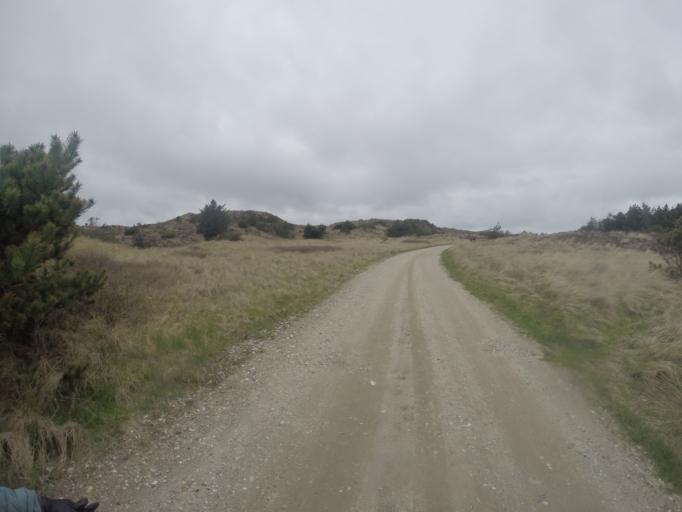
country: DK
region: North Denmark
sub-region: Thisted Kommune
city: Hurup
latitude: 56.8768
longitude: 8.3092
